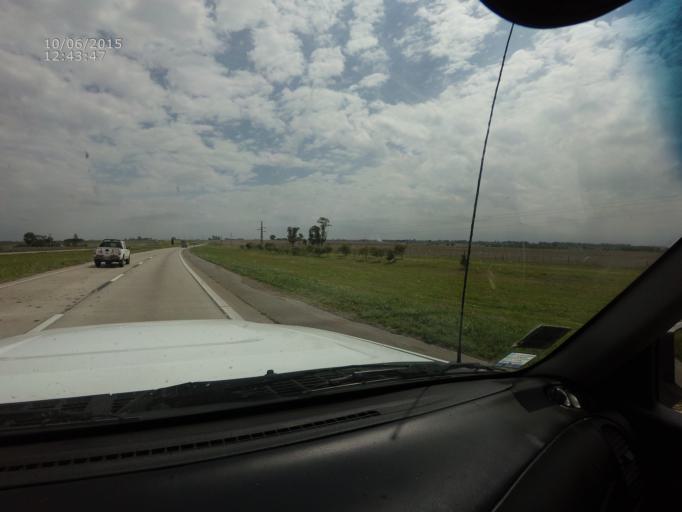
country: AR
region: Santa Fe
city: Canada de Gomez
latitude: -32.8540
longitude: -61.3545
